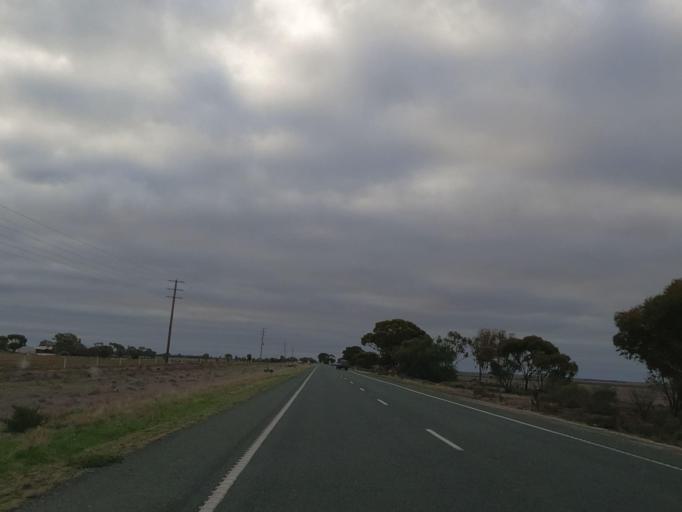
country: AU
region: Victoria
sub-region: Swan Hill
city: Swan Hill
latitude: -35.5803
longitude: 143.7892
